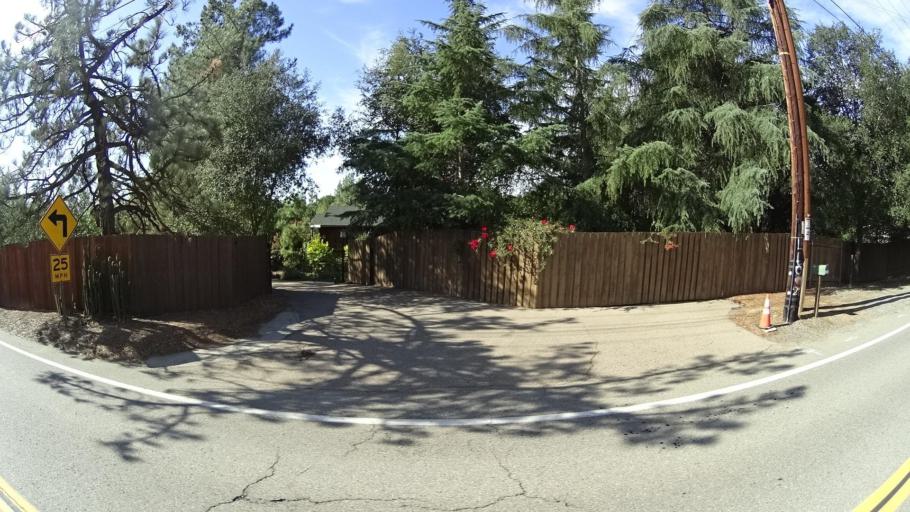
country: US
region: California
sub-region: San Diego County
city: Alpine
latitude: 32.8165
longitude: -116.7813
